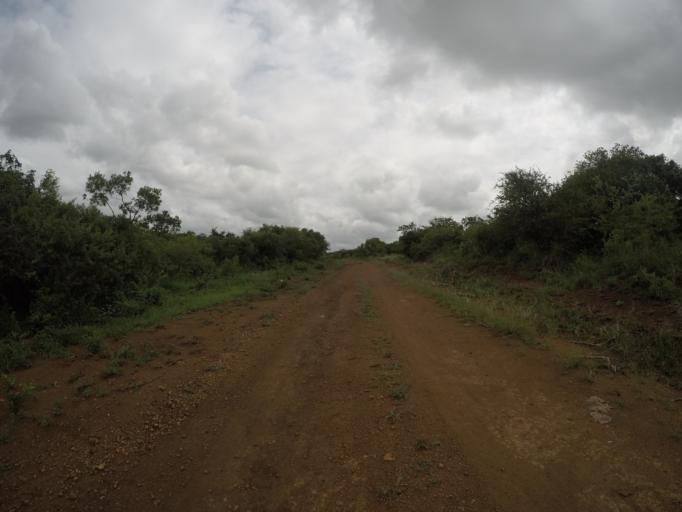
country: ZA
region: KwaZulu-Natal
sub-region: uThungulu District Municipality
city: Empangeni
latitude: -28.5857
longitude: 31.8689
